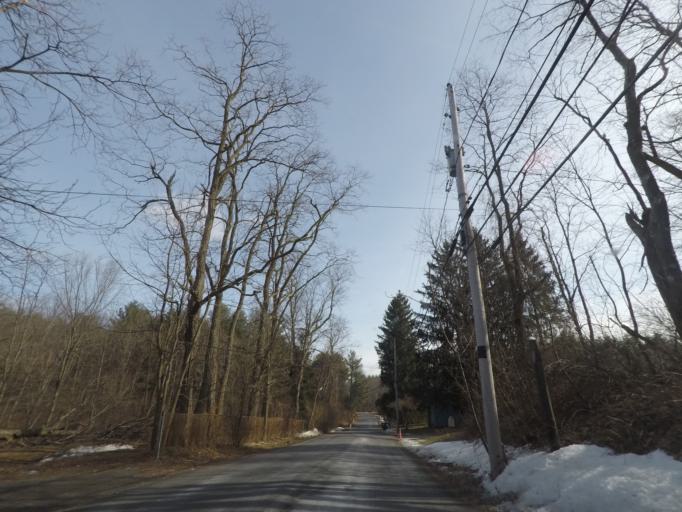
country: US
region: New York
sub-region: Rensselaer County
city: Nassau
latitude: 42.5076
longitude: -73.5593
